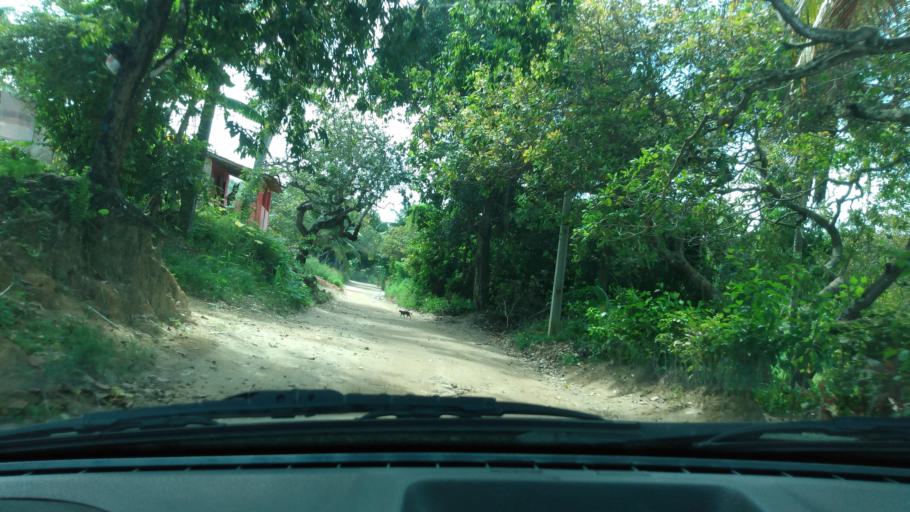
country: BR
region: Pernambuco
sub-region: Cabo De Santo Agostinho
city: Cabo
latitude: -8.3475
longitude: -34.9639
